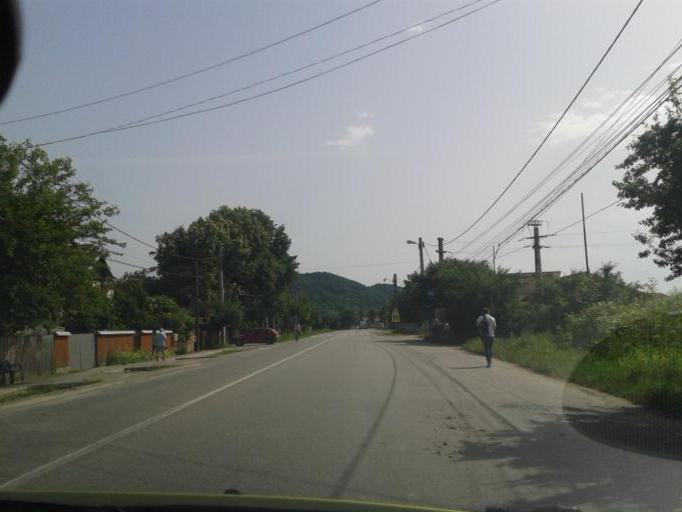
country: RO
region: Valcea
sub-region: Municipiul Ramnicu Valcea
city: Copacelu
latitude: 45.0671
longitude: 24.3096
